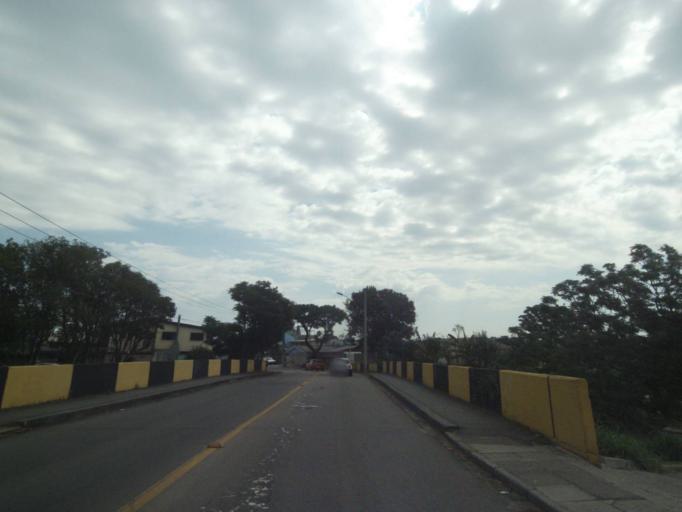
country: BR
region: Parana
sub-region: Sao Jose Dos Pinhais
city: Sao Jose dos Pinhais
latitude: -25.5230
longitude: -49.2672
